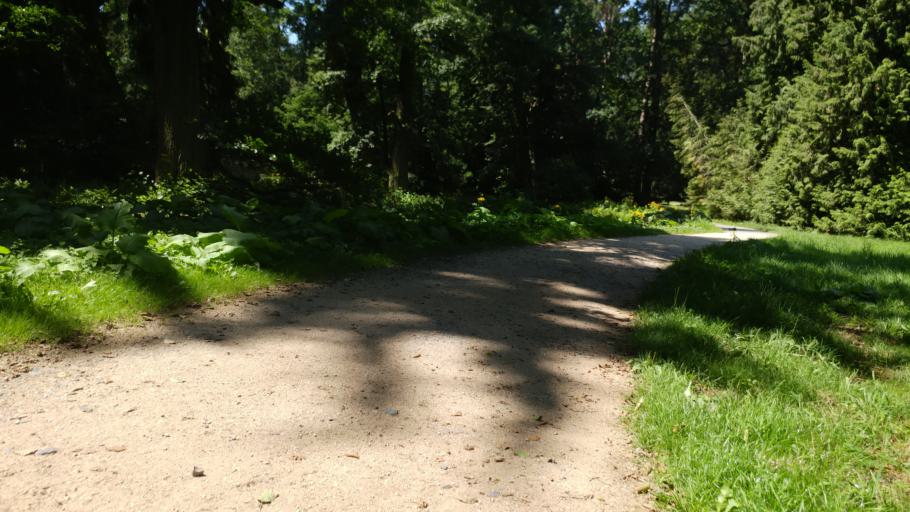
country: CZ
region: Central Bohemia
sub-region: Okres Praha-Zapad
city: Pruhonice
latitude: 49.9906
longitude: 14.5563
